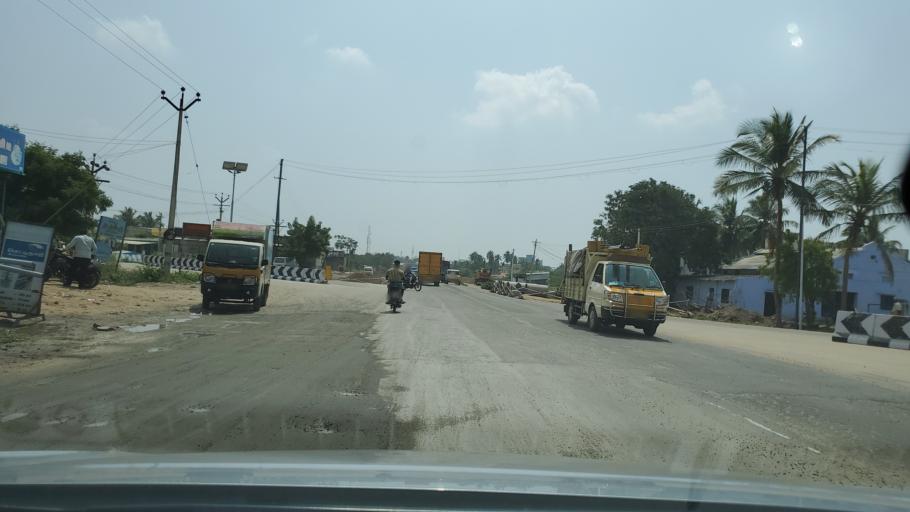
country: IN
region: Tamil Nadu
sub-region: Tiruppur
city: Dharapuram
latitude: 10.7478
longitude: 77.5188
